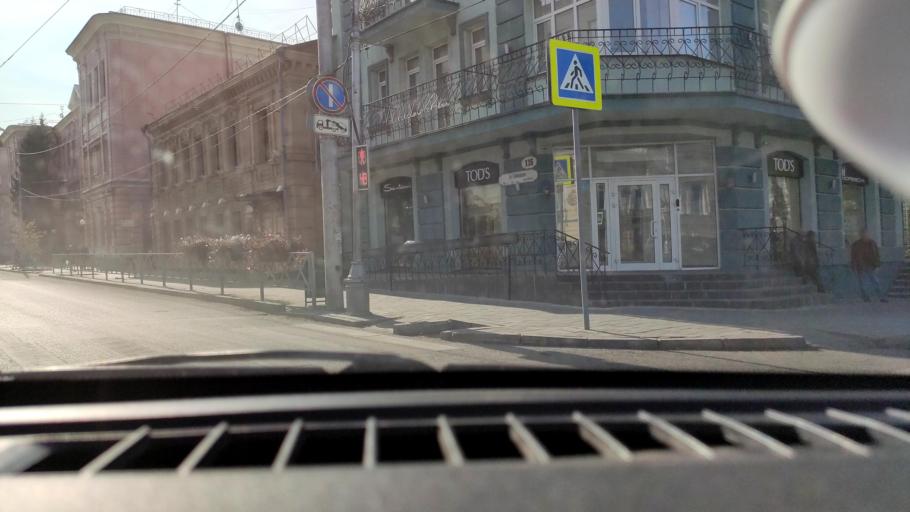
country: RU
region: Samara
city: Rozhdestveno
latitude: 53.1927
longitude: 50.0923
